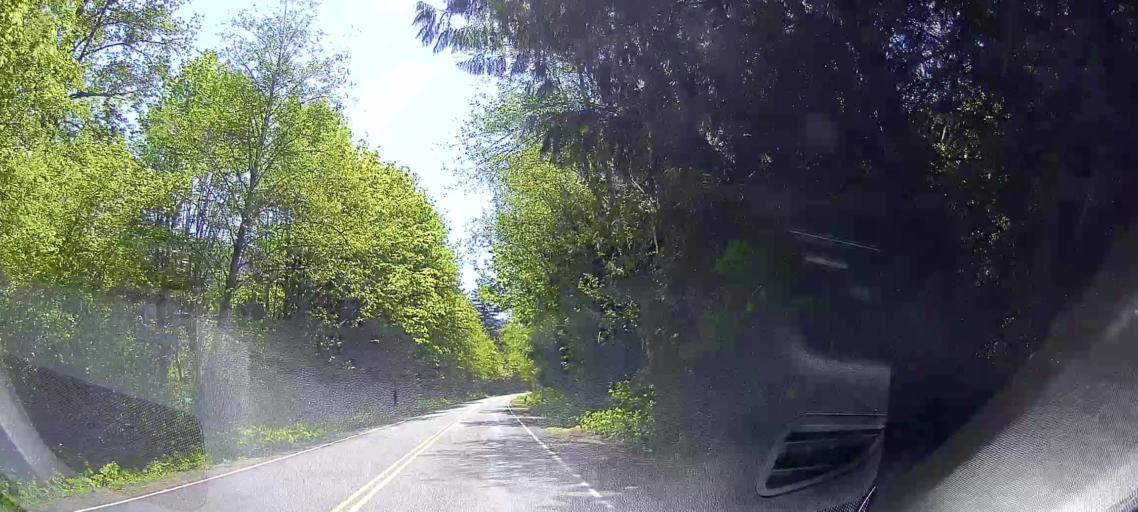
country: US
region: Washington
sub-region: Snohomish County
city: Darrington
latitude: 48.4321
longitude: -121.5743
